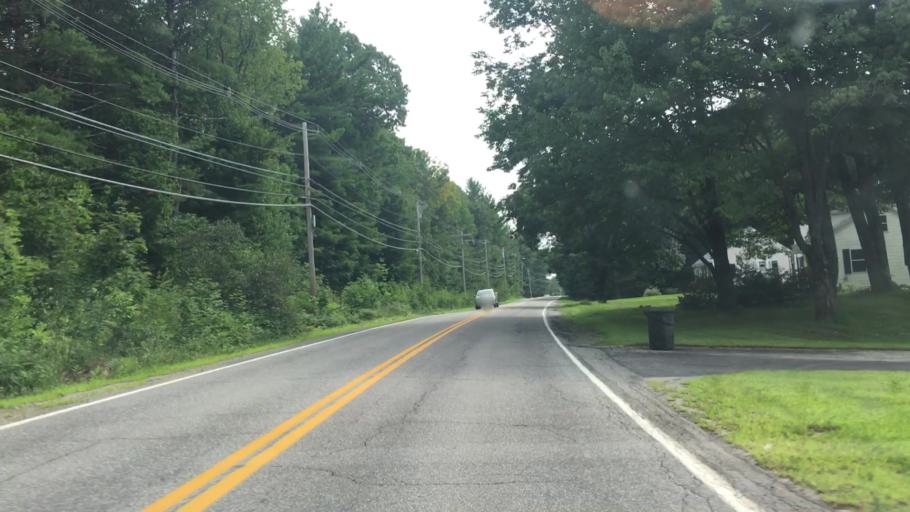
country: US
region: Maine
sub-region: Kennebec County
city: Winslow
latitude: 44.5204
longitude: -69.6308
